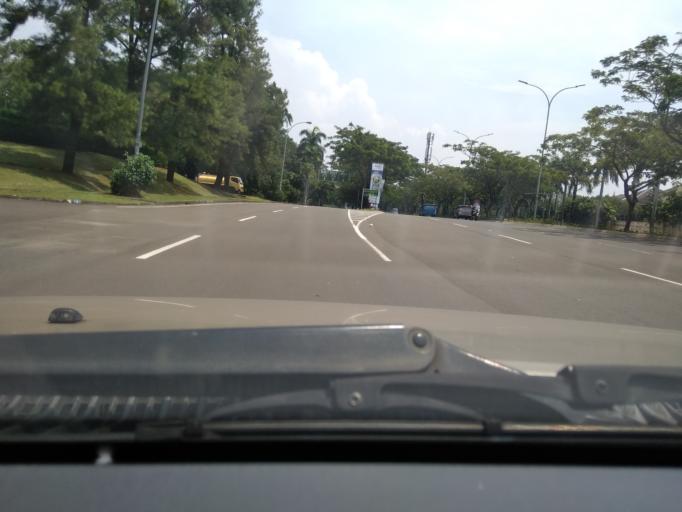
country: ID
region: West Java
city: Serpong
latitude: -6.2806
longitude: 106.6599
